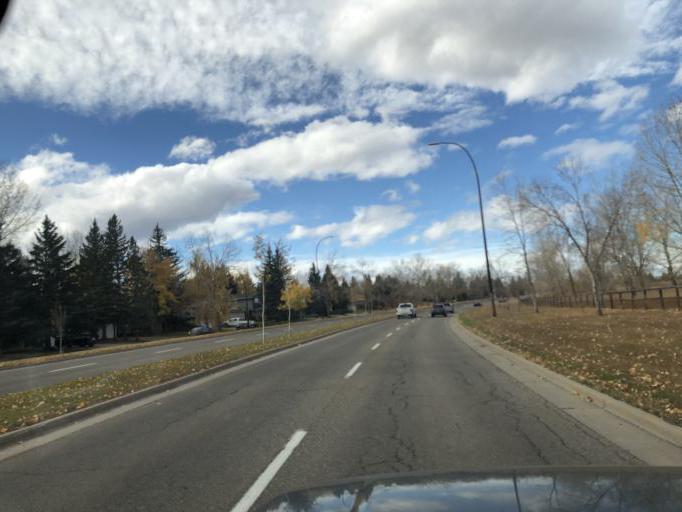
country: CA
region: Alberta
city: Calgary
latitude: 50.9725
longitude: -114.1223
